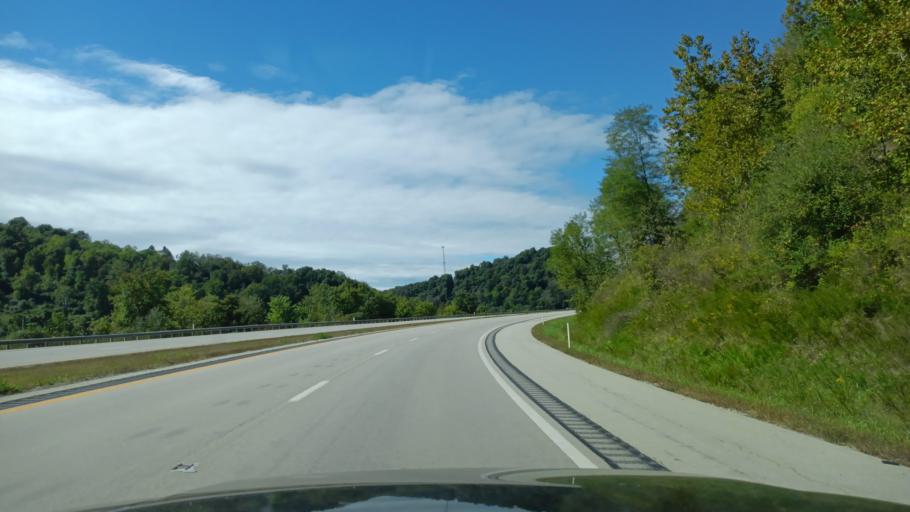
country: US
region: West Virginia
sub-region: Doddridge County
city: West Union
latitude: 39.2788
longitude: -80.6877
